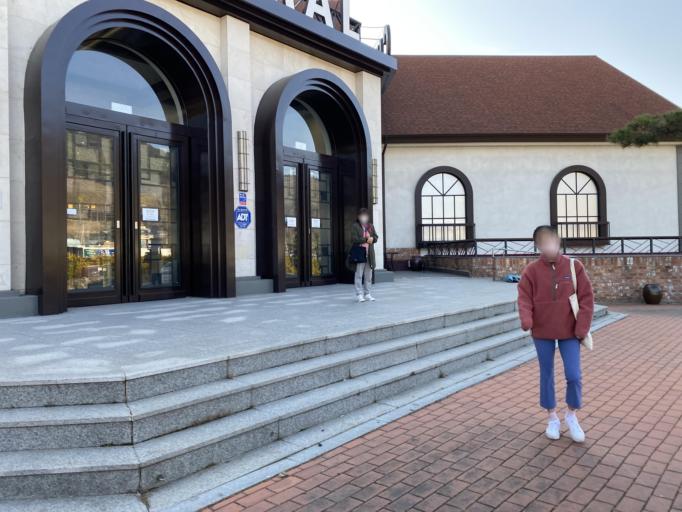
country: KR
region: Chungcheongnam-do
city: Yesan
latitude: 36.6795
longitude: 126.8604
